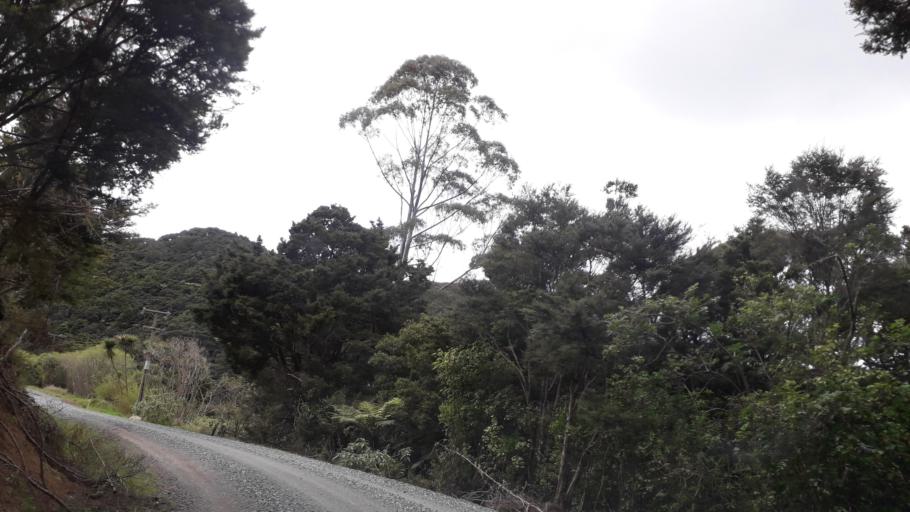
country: NZ
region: Northland
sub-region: Far North District
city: Taipa
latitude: -35.0800
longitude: 173.5551
